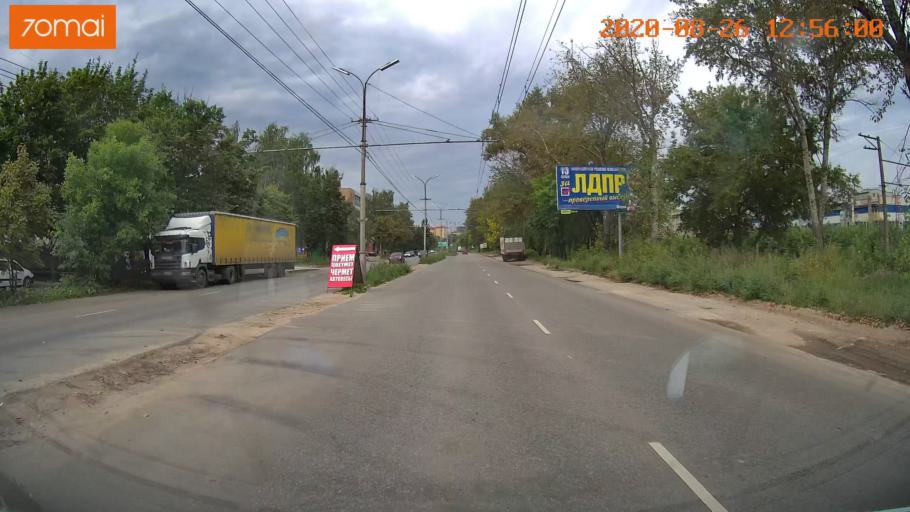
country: RU
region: Rjazan
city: Ryazan'
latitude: 54.6115
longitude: 39.7549
